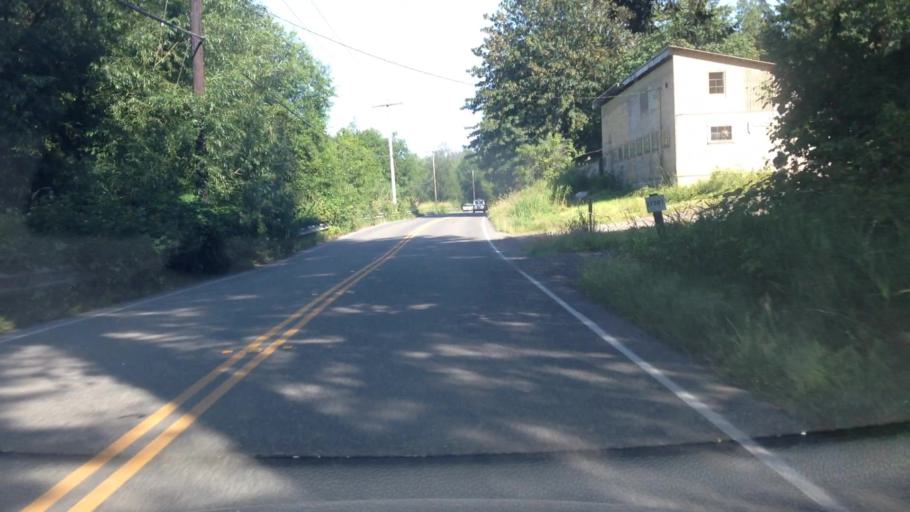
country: US
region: Washington
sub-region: King County
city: Duvall
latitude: 47.7510
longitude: -121.9684
